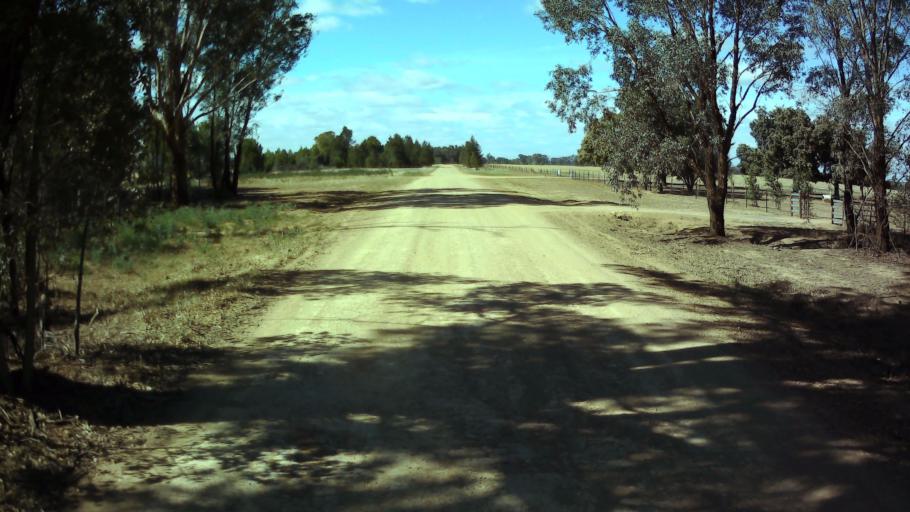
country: AU
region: New South Wales
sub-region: Weddin
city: Grenfell
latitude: -34.0295
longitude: 148.3175
